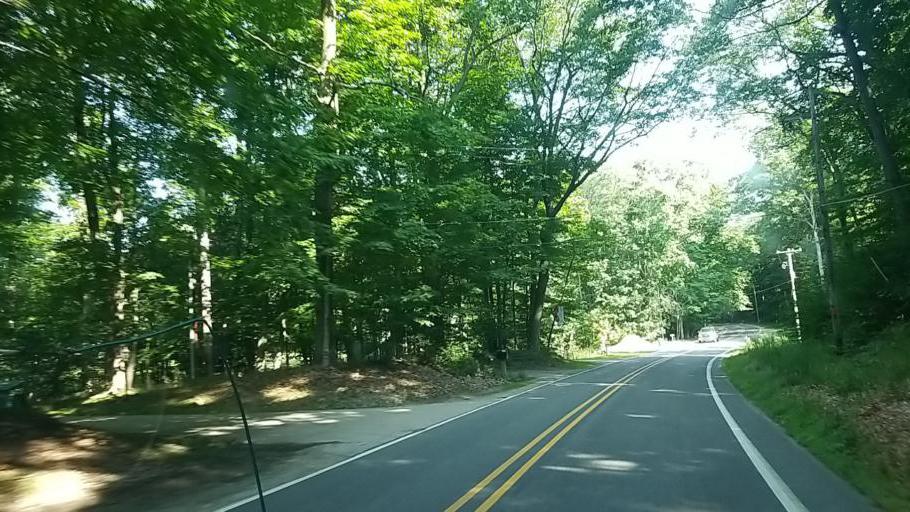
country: US
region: Michigan
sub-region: Muskegon County
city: Whitehall
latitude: 43.3210
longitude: -86.3957
